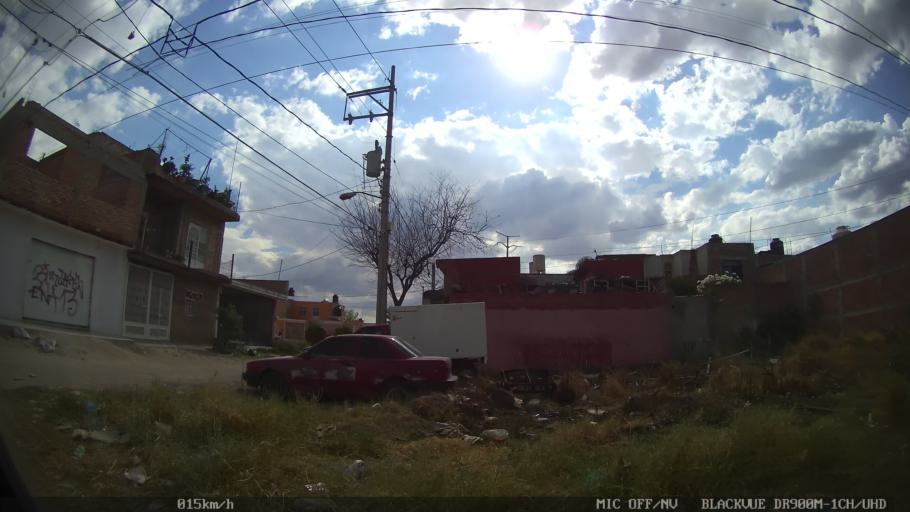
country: MX
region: Jalisco
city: Tlaquepaque
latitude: 20.6638
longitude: -103.2661
